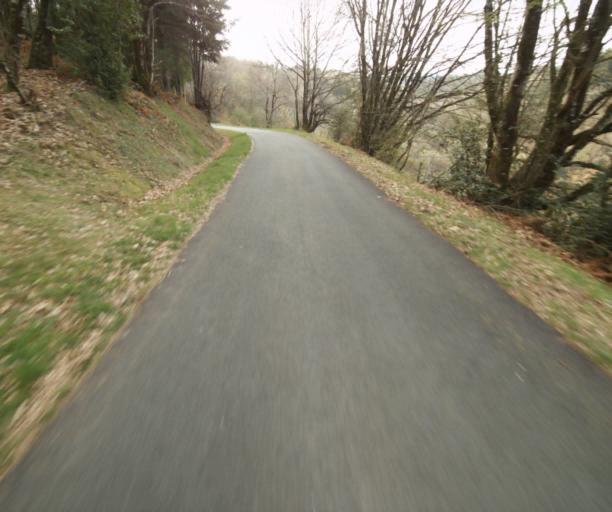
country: FR
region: Limousin
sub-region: Departement de la Correze
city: Chamboulive
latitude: 45.4341
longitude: 1.7886
